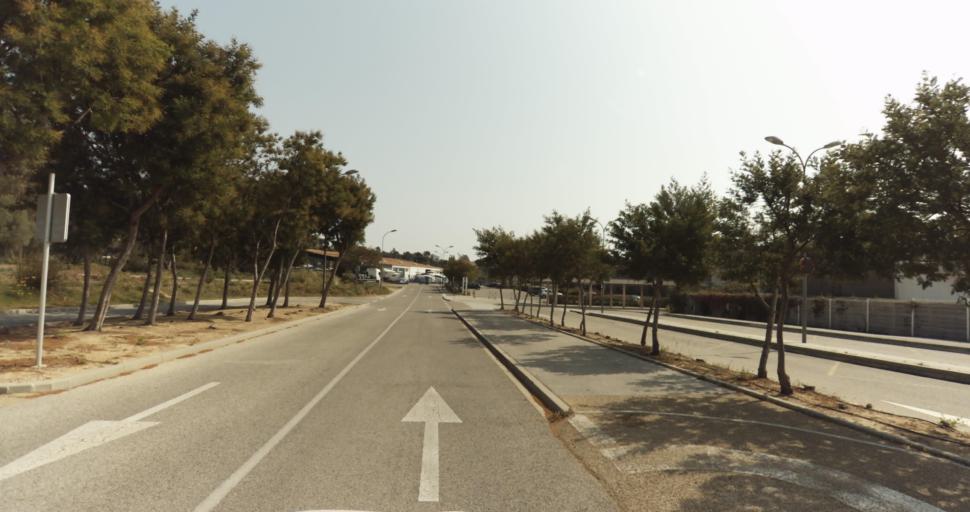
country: FR
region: Provence-Alpes-Cote d'Azur
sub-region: Departement du Var
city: Bormes-les-Mimosas
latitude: 43.1414
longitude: 6.3465
